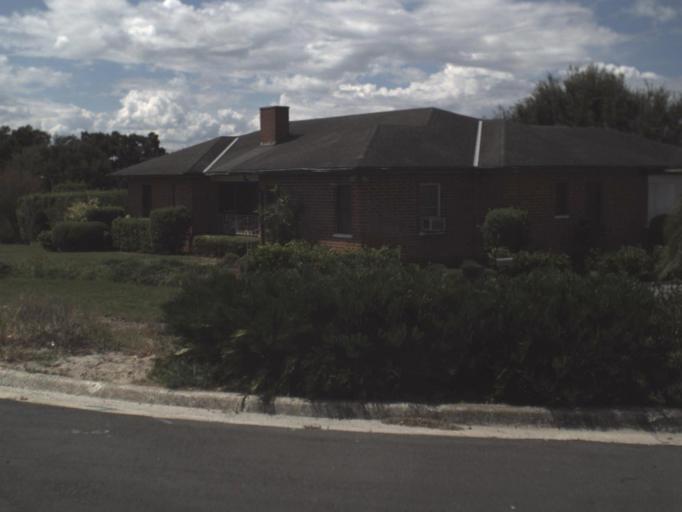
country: US
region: Florida
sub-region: Polk County
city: Lake Wales
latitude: 27.8941
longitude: -81.5741
